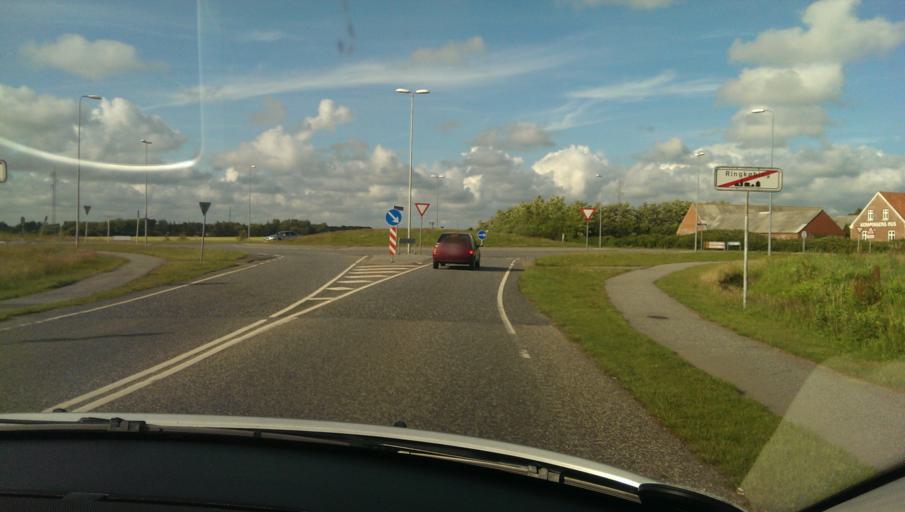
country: DK
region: Central Jutland
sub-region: Ringkobing-Skjern Kommune
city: Ringkobing
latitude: 56.1051
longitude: 8.2589
